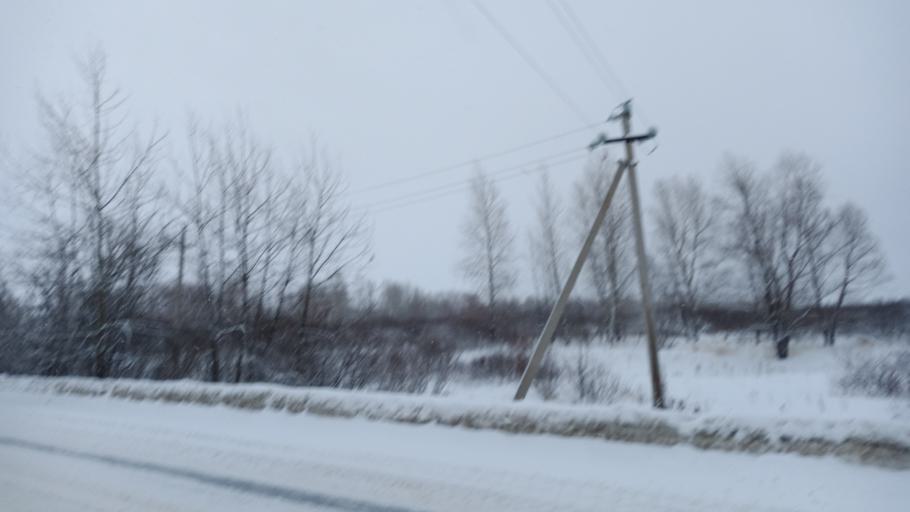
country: RU
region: Altai Krai
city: Zaton
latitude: 53.3123
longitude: 83.8310
